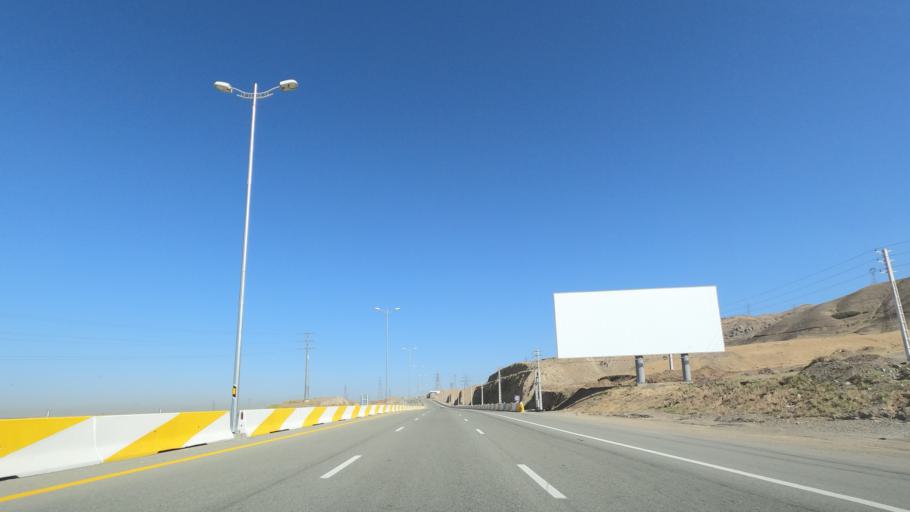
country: IR
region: Tehran
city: Shahr-e Qods
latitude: 35.7704
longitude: 51.0606
